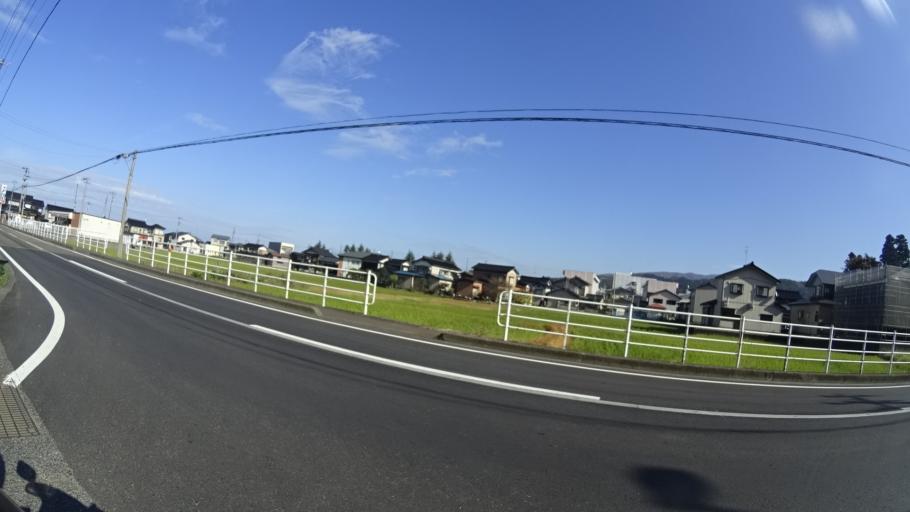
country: JP
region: Niigata
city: Itoigawa
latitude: 37.0405
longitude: 137.8829
